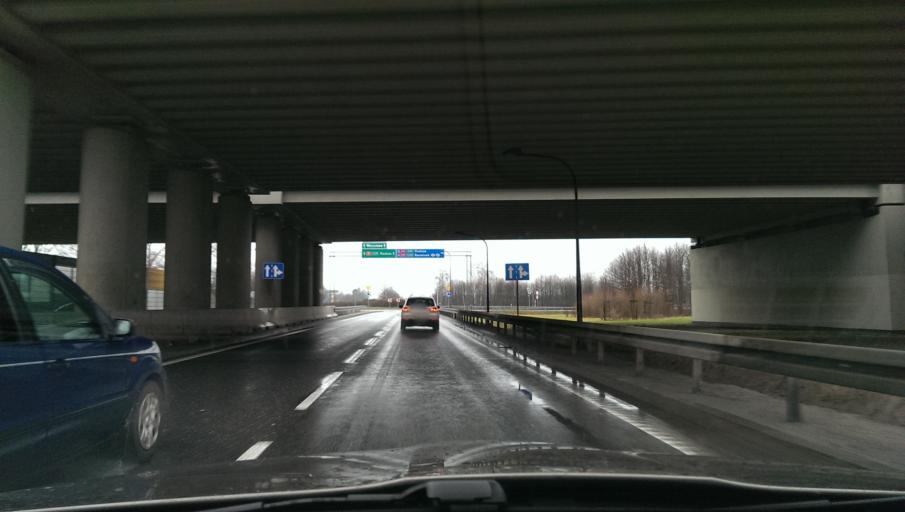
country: PL
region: Subcarpathian Voivodeship
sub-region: Powiat rzeszowski
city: Rudna Mala
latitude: 50.1075
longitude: 21.9761
